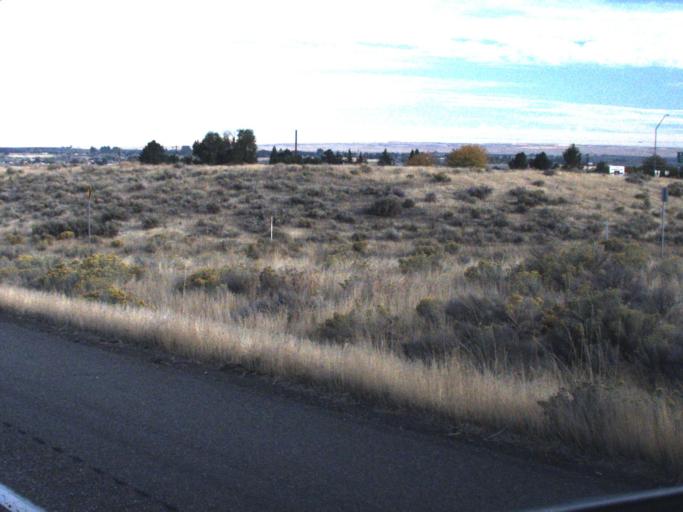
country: US
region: Washington
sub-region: Benton County
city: Prosser
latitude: 46.2129
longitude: -119.7406
